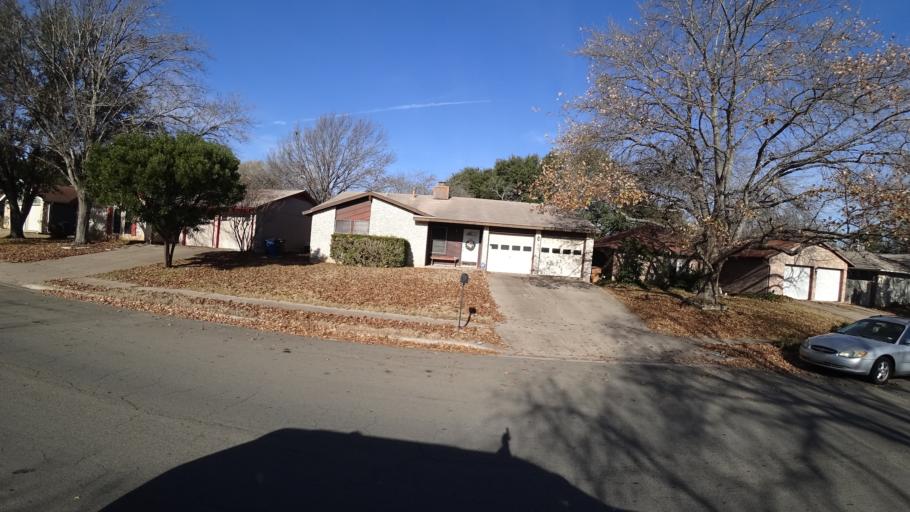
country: US
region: Texas
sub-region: Travis County
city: Wells Branch
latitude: 30.3918
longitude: -97.6991
